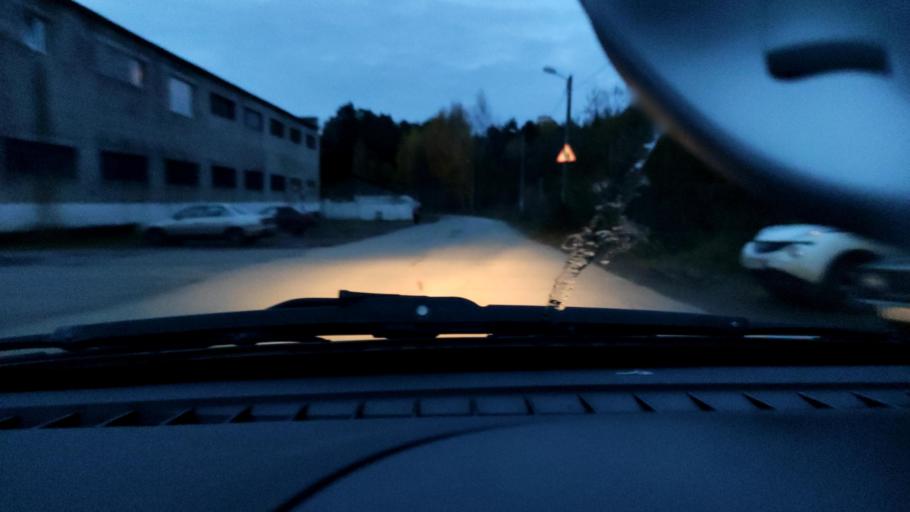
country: RU
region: Perm
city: Kondratovo
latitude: 58.0446
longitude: 56.1380
